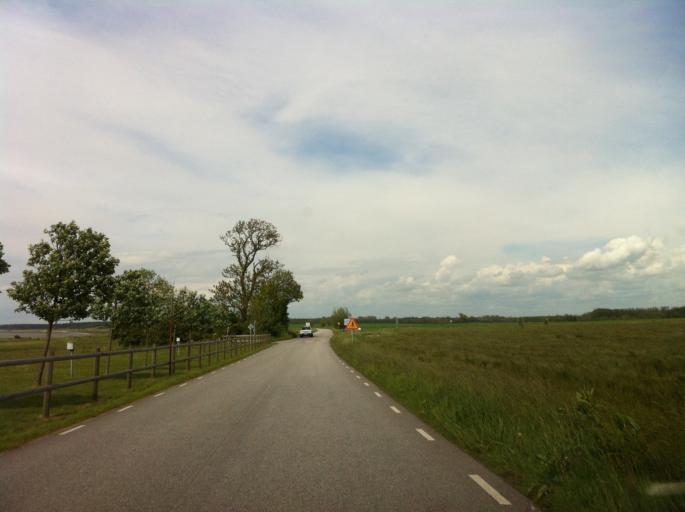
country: SE
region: Skane
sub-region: Kavlinge Kommun
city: Hofterup
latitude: 55.7707
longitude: 12.9290
